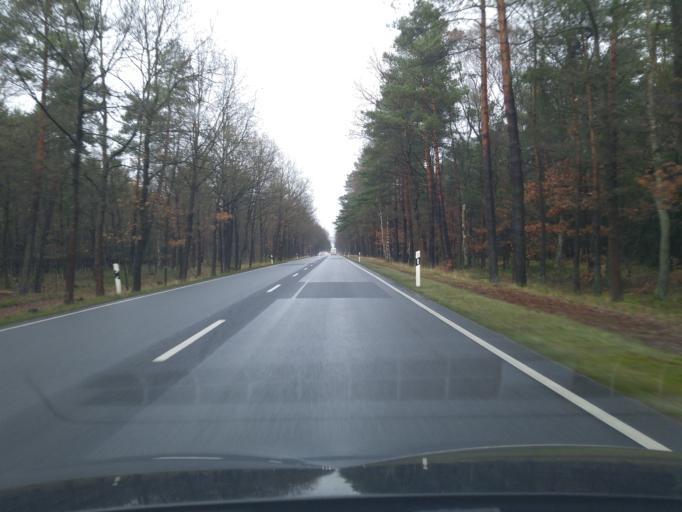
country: DE
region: Lower Saxony
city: Dedelstorf
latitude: 52.7227
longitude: 10.4827
